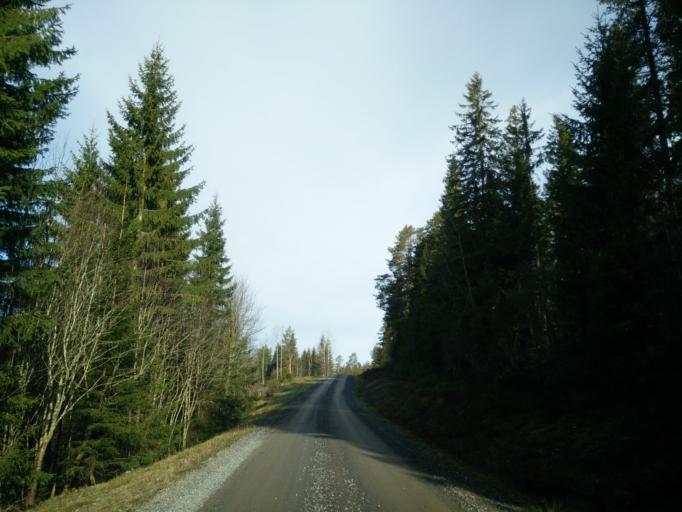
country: SE
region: Vaesternorrland
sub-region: Haernoesands Kommun
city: Haernoesand
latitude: 62.6107
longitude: 17.7194
